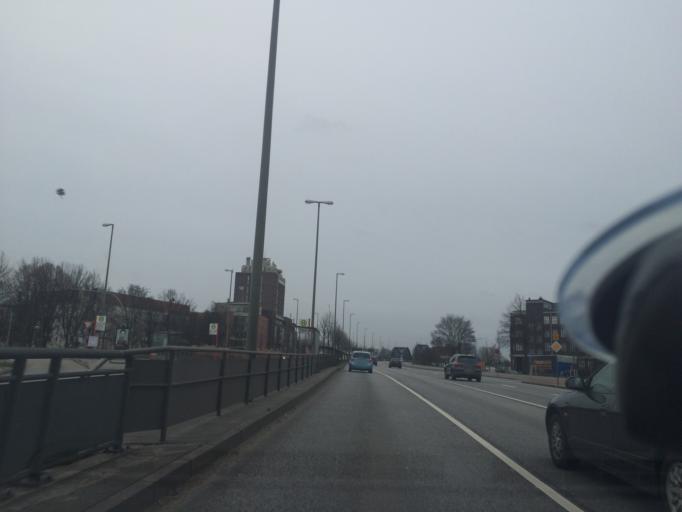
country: DE
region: Hamburg
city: Hammerbrook
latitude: 53.5384
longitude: 10.0310
